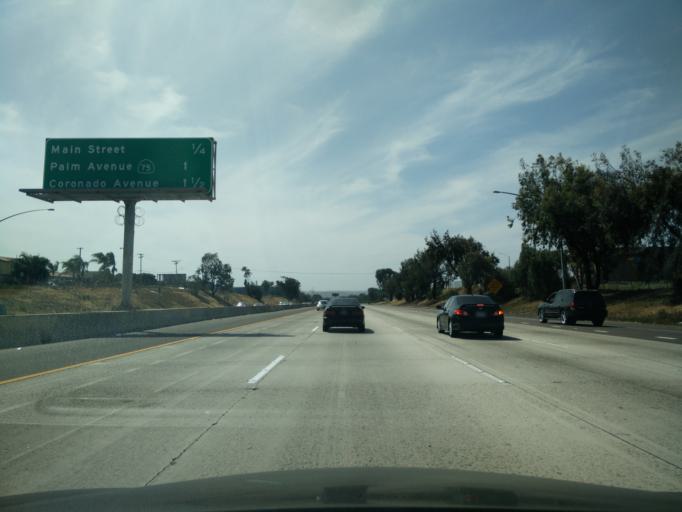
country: US
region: California
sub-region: San Diego County
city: Imperial Beach
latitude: 32.6020
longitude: -117.0898
